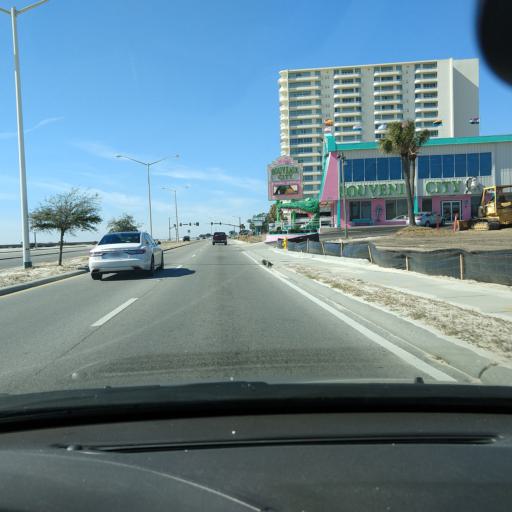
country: US
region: Mississippi
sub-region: Harrison County
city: Biloxi
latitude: 30.3925
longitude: -88.9571
